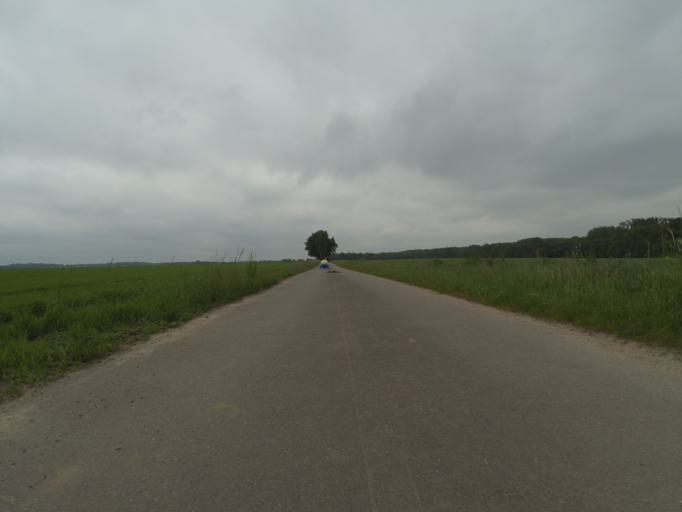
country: DE
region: Lower Saxony
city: Edemissen
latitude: 52.3721
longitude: 10.3192
